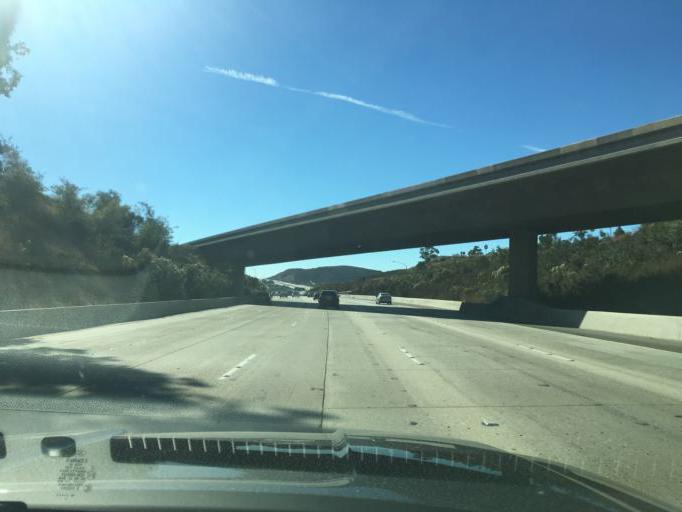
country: US
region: California
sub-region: San Diego County
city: Poway
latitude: 32.9587
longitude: -117.0998
